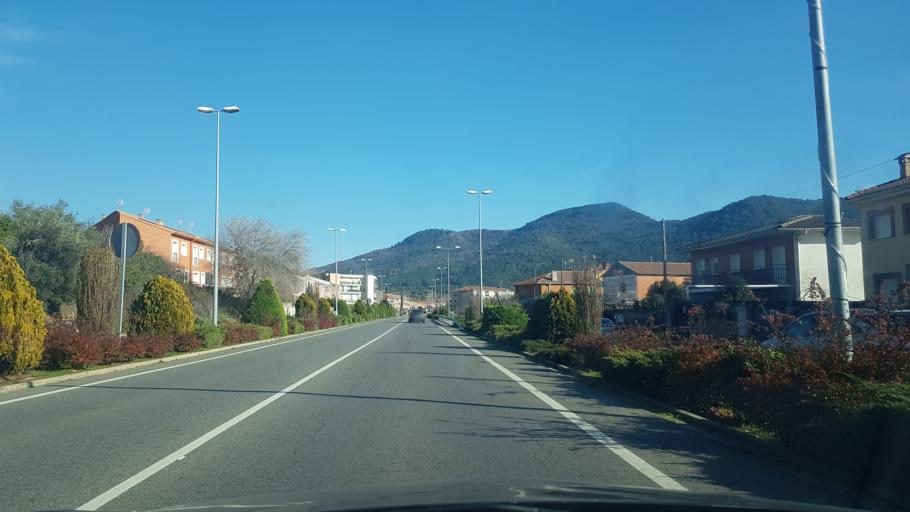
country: ES
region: Castille and Leon
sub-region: Provincia de Avila
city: Casillas
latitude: 40.3022
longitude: -4.5557
